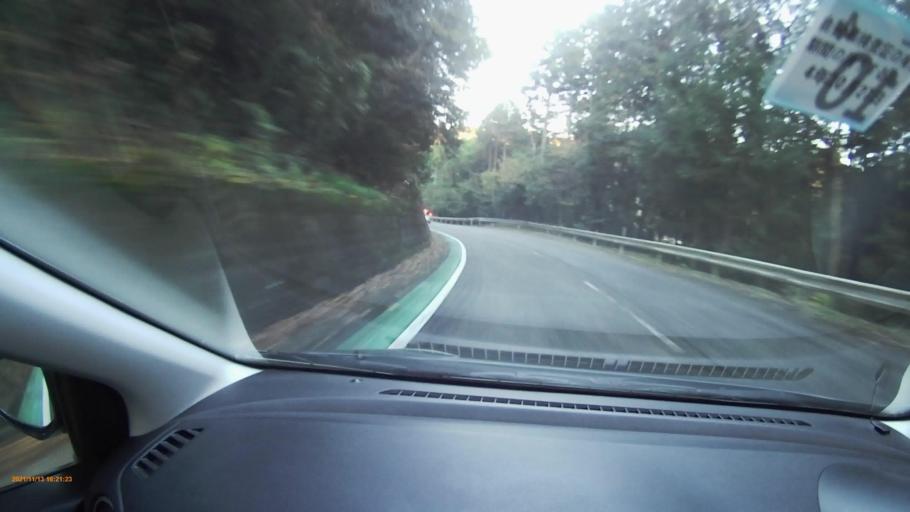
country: JP
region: Gifu
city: Nakatsugawa
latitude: 35.5661
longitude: 137.5232
